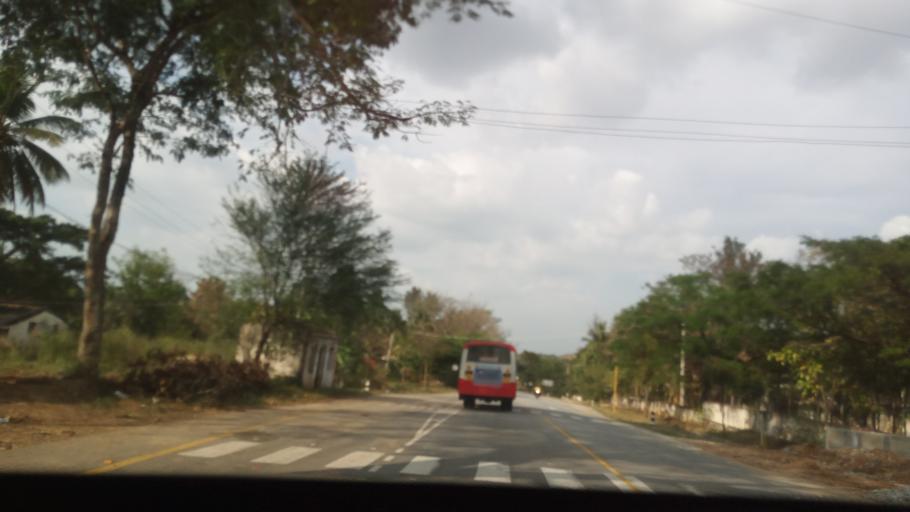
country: IN
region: Karnataka
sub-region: Tumkur
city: Kunigal
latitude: 12.8544
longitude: 77.0386
